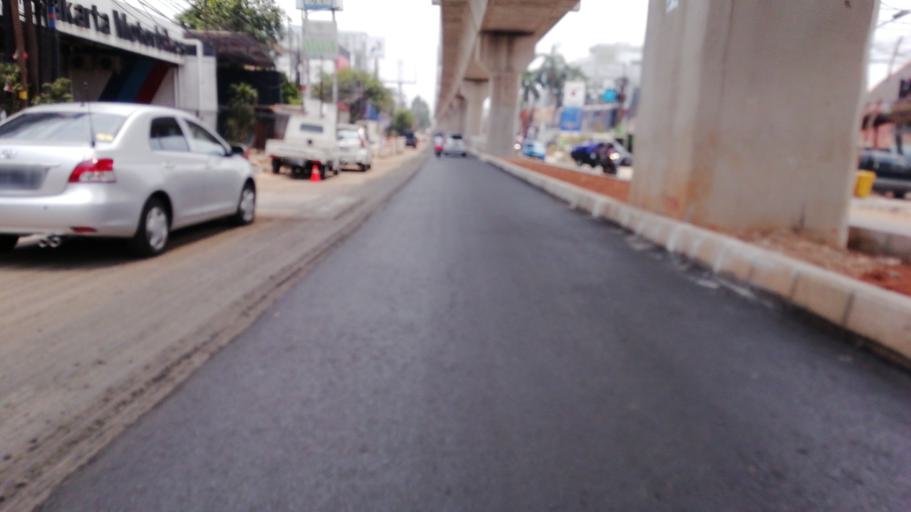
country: ID
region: Jakarta Raya
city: Jakarta
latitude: -6.2731
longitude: 106.7976
